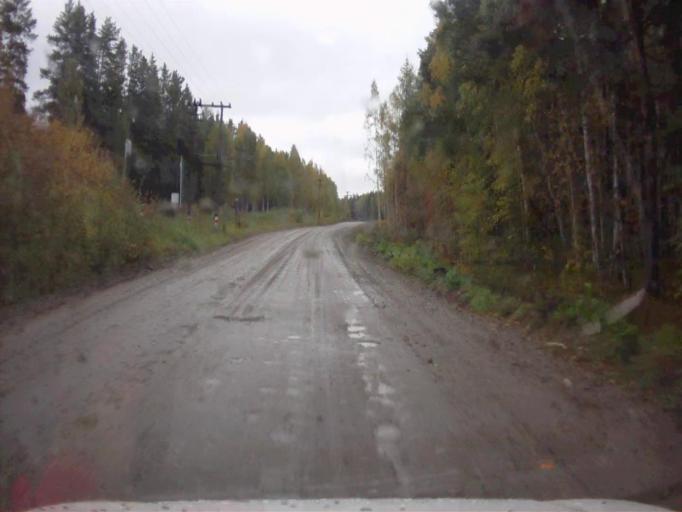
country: RU
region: Chelyabinsk
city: Kyshtym
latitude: 55.8015
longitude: 60.4798
